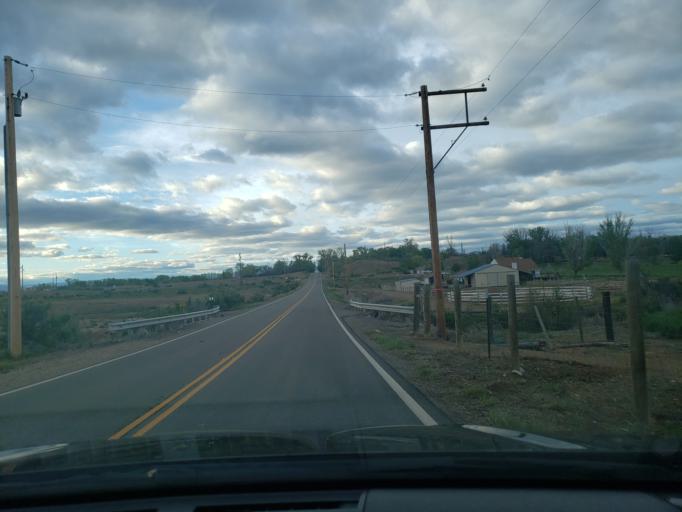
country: US
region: Colorado
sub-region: Mesa County
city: Fruita
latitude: 39.1872
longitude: -108.7291
